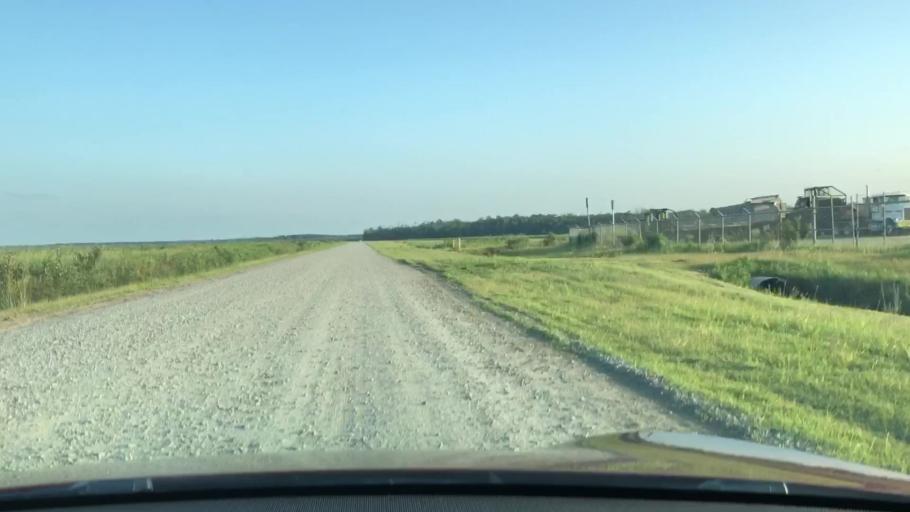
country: US
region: North Carolina
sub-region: Dare County
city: Manteo
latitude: 35.8542
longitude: -75.8623
